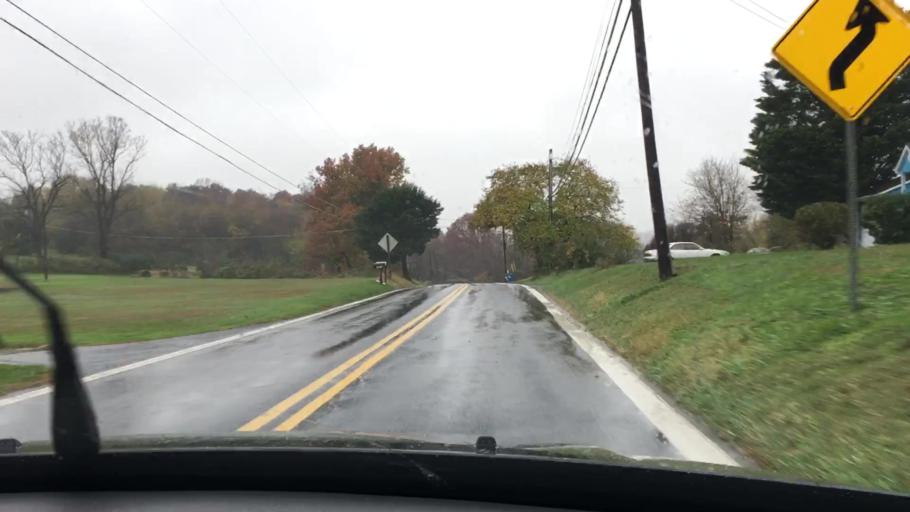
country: US
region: Maryland
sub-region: Frederick County
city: Buckeystown
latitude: 39.3340
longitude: -77.3952
